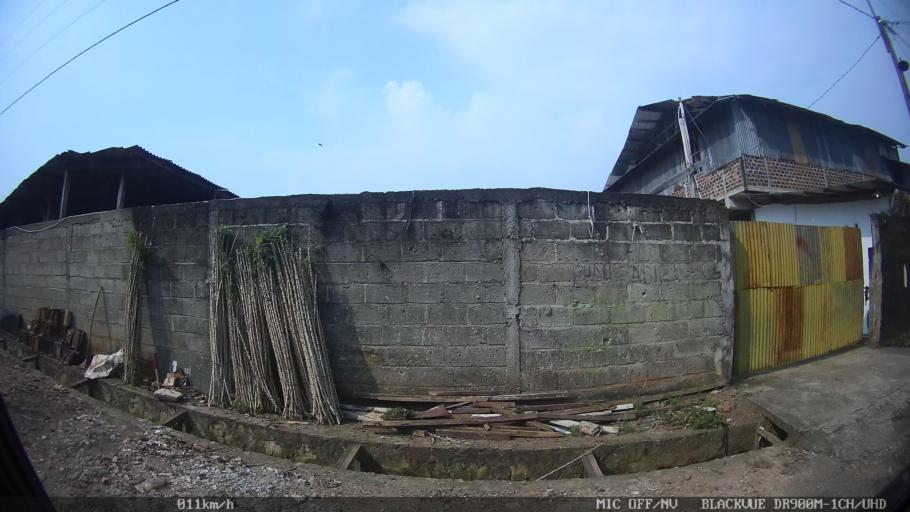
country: ID
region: Lampung
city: Kedaton
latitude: -5.3619
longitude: 105.2170
